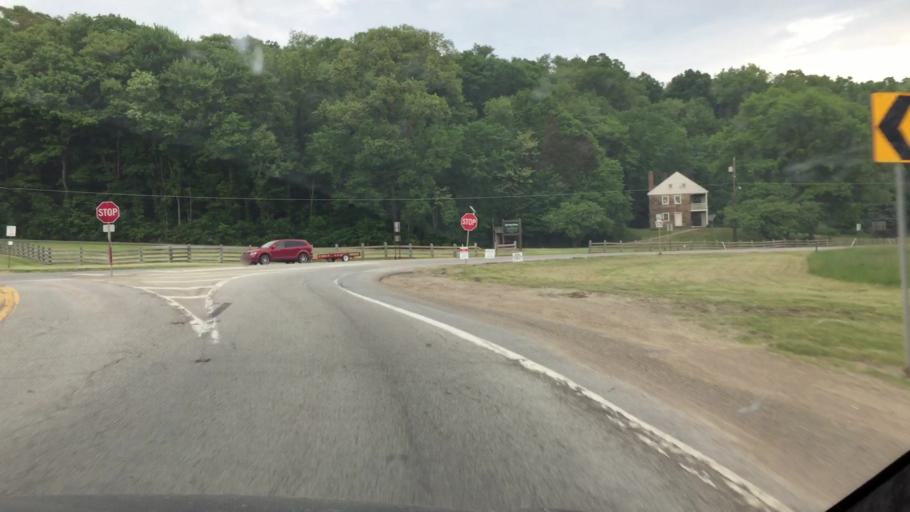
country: US
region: Pennsylvania
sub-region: Butler County
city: Slippery Rock
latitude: 41.0123
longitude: -80.0035
